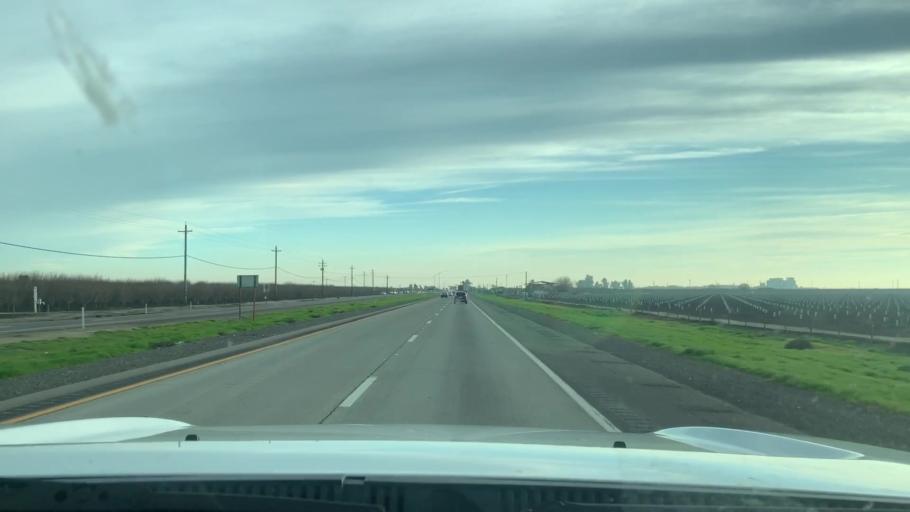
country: US
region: California
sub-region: Kings County
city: Lemoore
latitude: 36.3195
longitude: -119.8081
